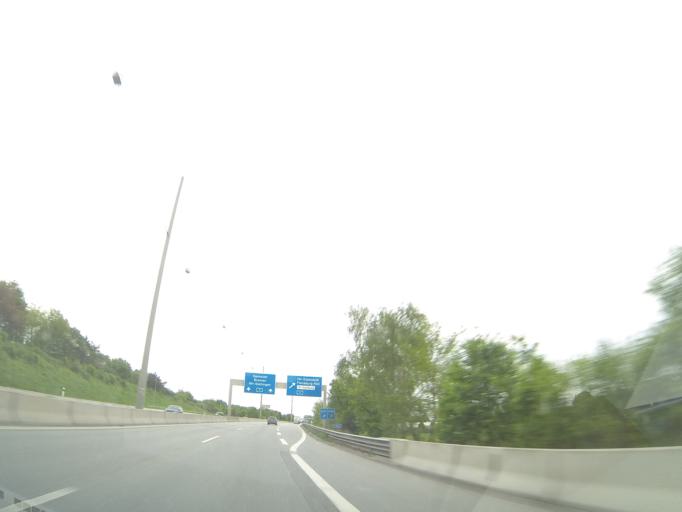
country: DE
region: Hamburg
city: Eidelstedt
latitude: 53.6216
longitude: 9.9011
